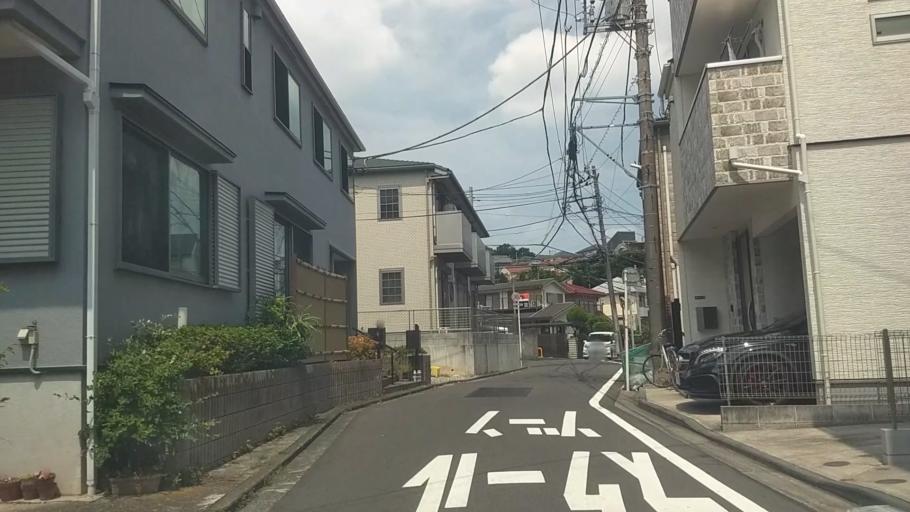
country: JP
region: Kanagawa
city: Yokohama
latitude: 35.5088
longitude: 139.6248
